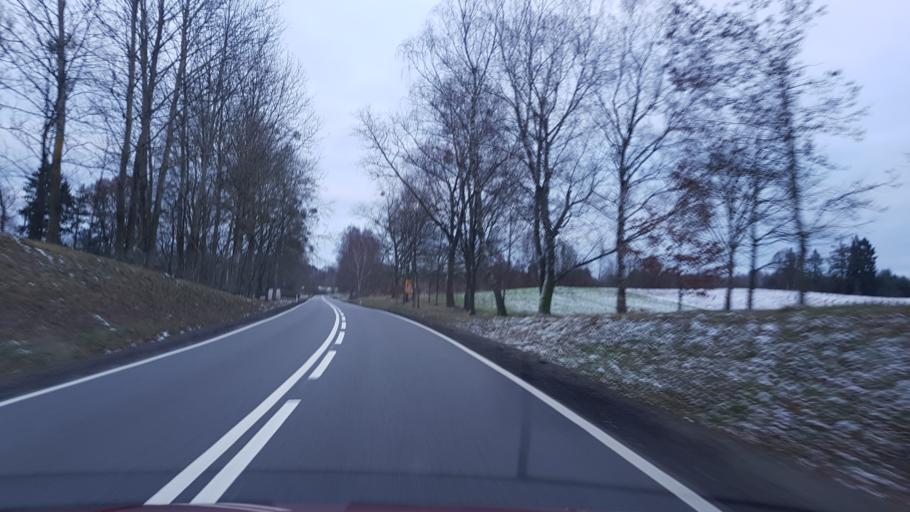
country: PL
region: Pomeranian Voivodeship
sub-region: Powiat bytowski
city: Tuchomie
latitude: 54.0501
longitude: 17.2146
